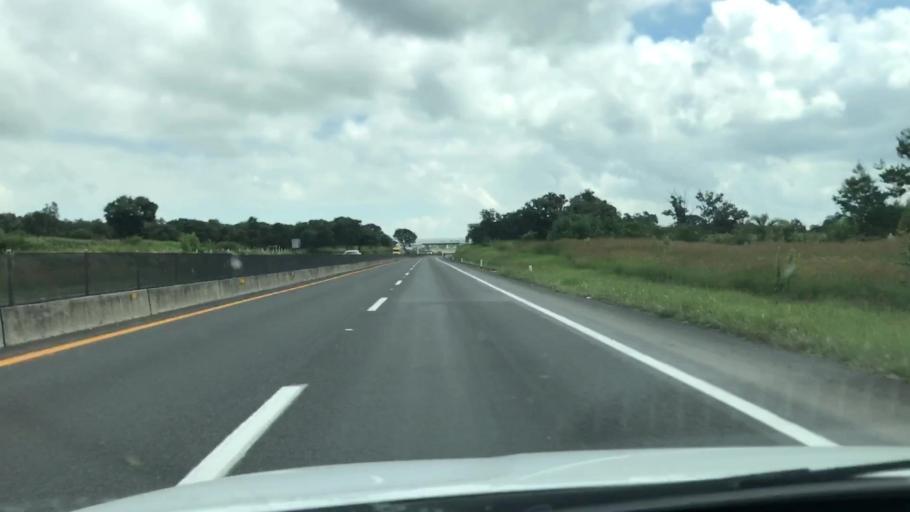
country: MX
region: Jalisco
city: Tepatitlan de Morelos
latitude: 20.8647
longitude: -102.7594
